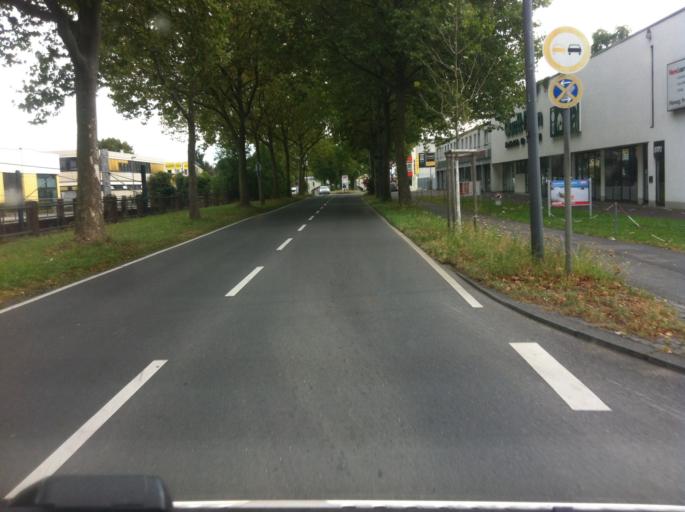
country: DE
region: North Rhine-Westphalia
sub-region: Regierungsbezirk Koln
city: Mengenich
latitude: 50.9643
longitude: 6.8861
